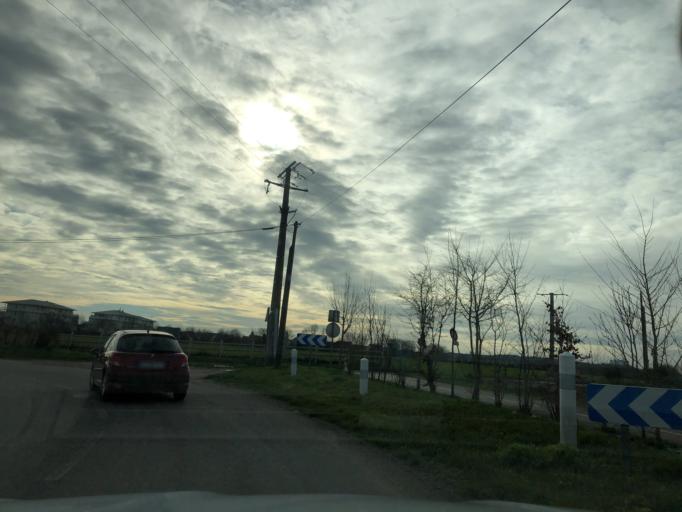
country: FR
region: Lower Normandy
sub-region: Departement du Calvados
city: Blainville-sur-Orne
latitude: 49.2332
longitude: -0.3098
